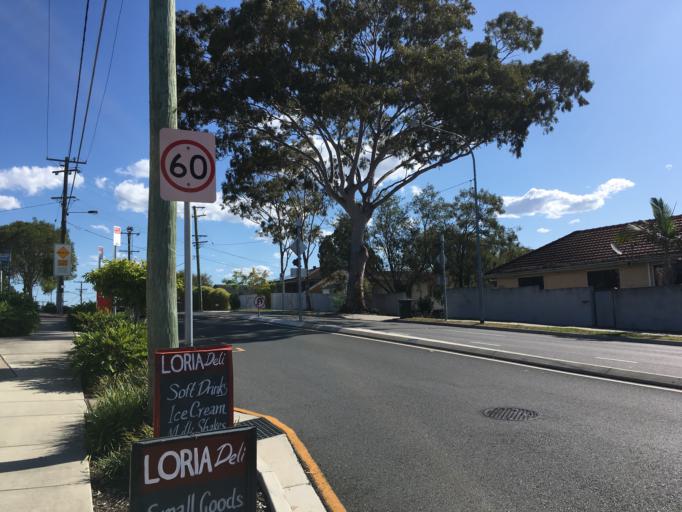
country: AU
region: Queensland
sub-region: Brisbane
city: Chermside West
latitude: -27.3842
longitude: 153.0127
